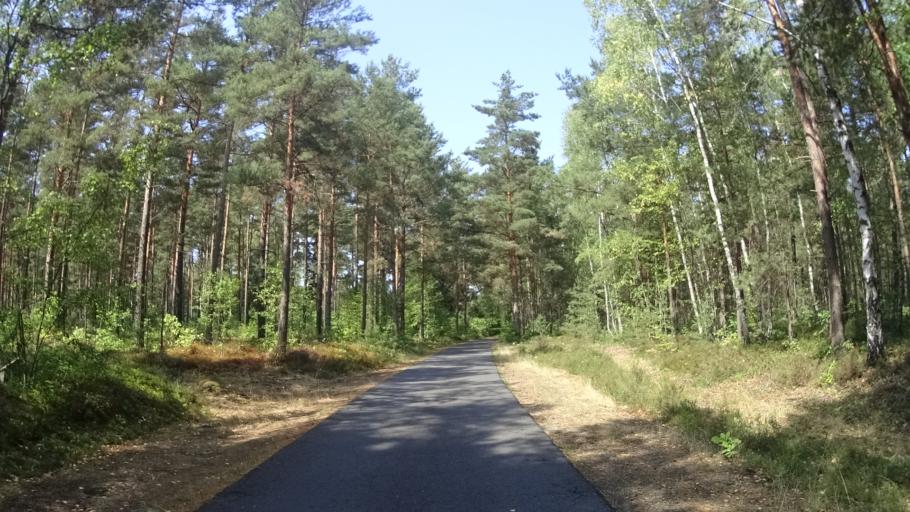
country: DE
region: Brandenburg
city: Tschernitz
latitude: 51.5976
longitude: 14.5930
